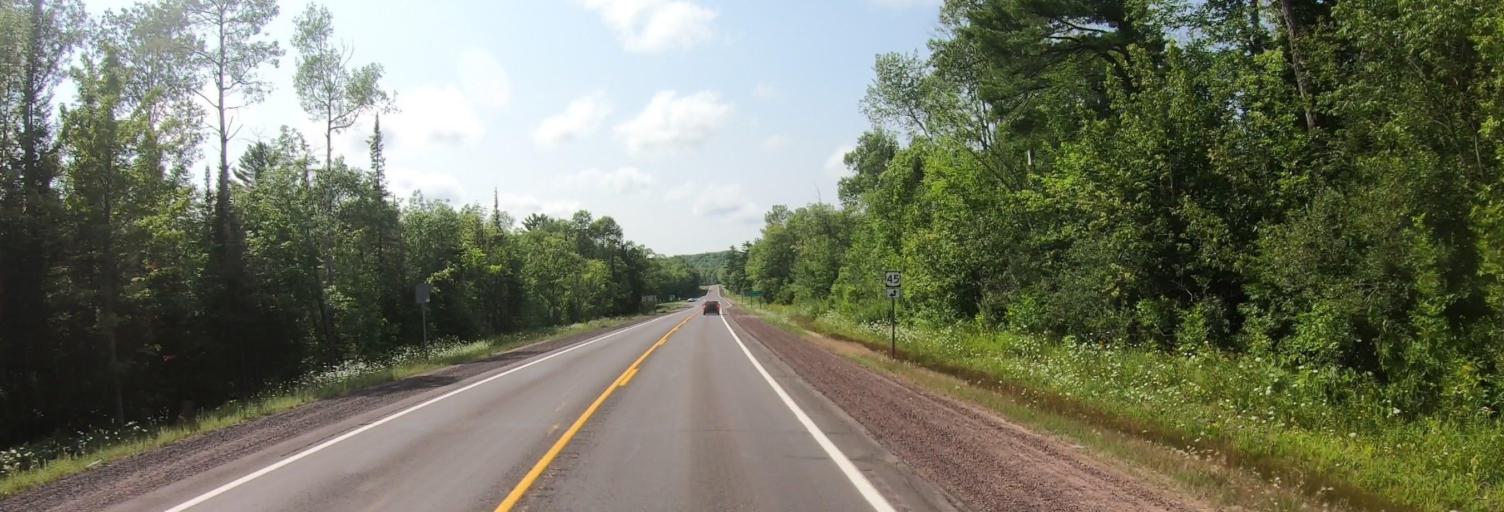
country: US
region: Michigan
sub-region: Ontonagon County
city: Ontonagon
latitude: 46.7298
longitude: -89.1436
